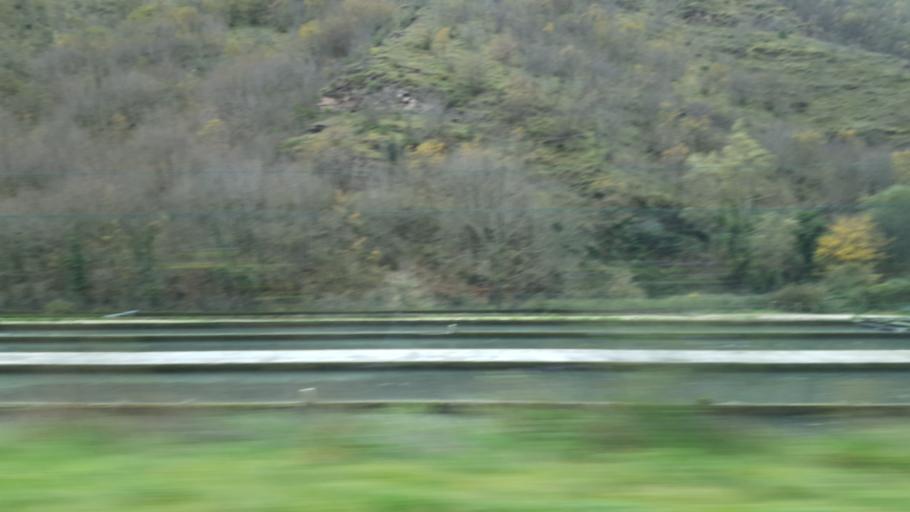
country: IT
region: The Marches
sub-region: Provincia di Macerata
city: Visso
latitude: 42.9256
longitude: 13.1018
